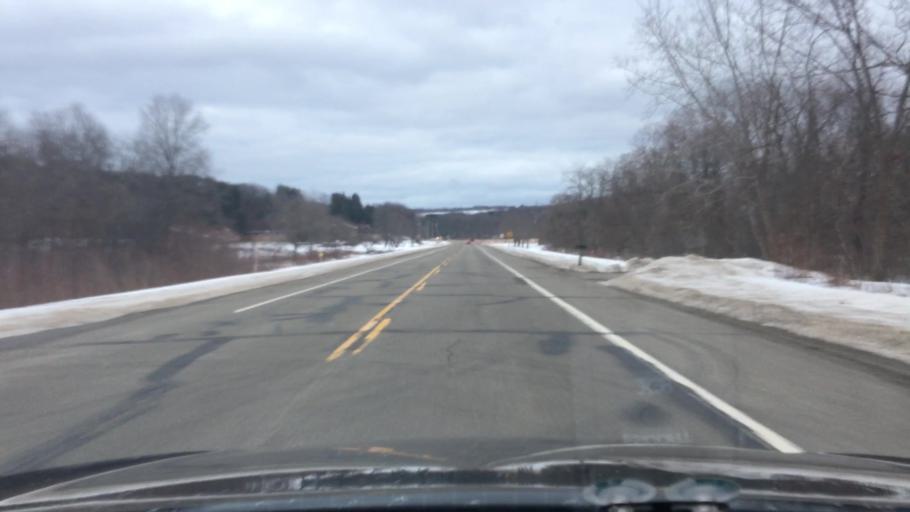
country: US
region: New York
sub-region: Chautauqua County
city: Lakewood
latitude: 42.1690
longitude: -79.3829
